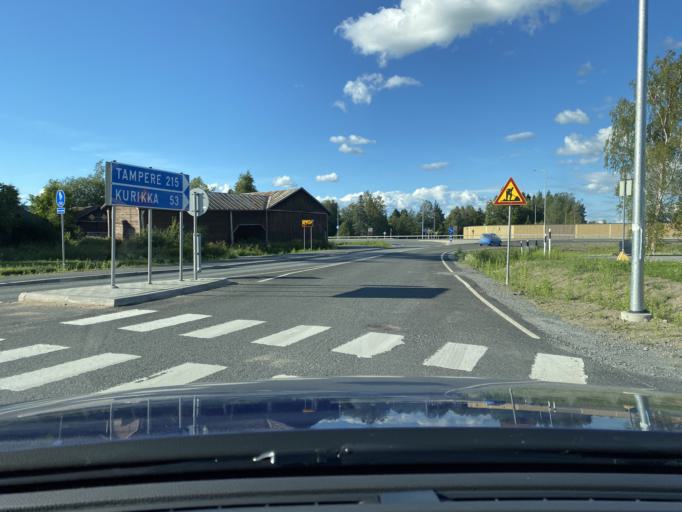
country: FI
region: Ostrobothnia
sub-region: Kyroenmaa
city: Laihia
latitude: 62.9829
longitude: 22.0004
